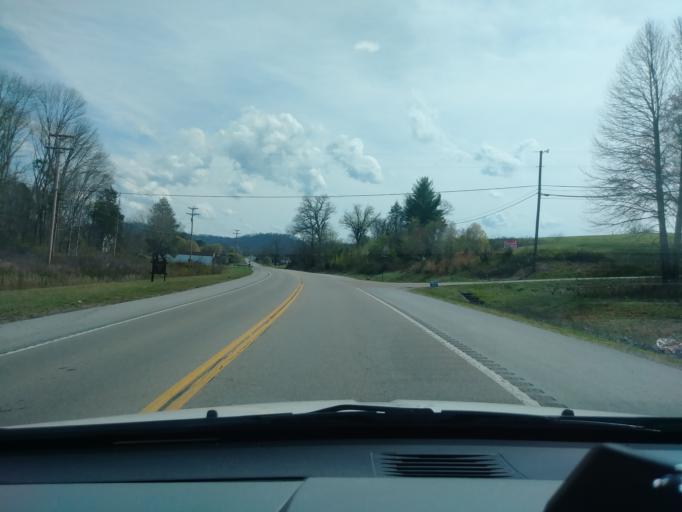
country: US
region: Tennessee
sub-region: Greene County
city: Greeneville
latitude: 36.0631
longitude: -82.8672
